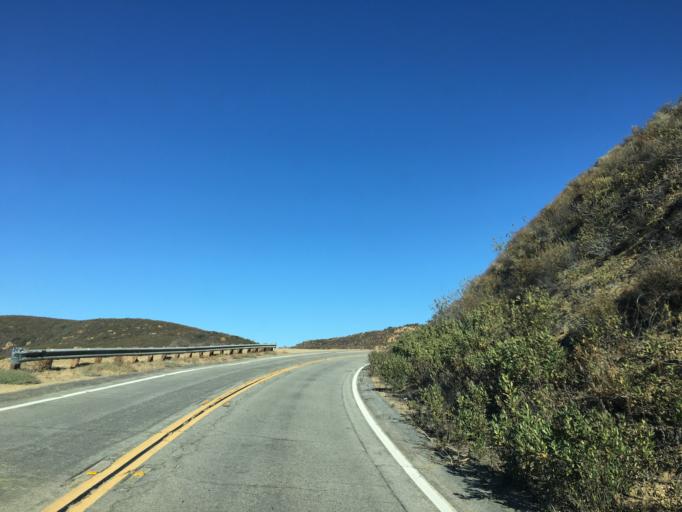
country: US
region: California
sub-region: Los Angeles County
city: Castaic
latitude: 34.5601
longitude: -118.5490
